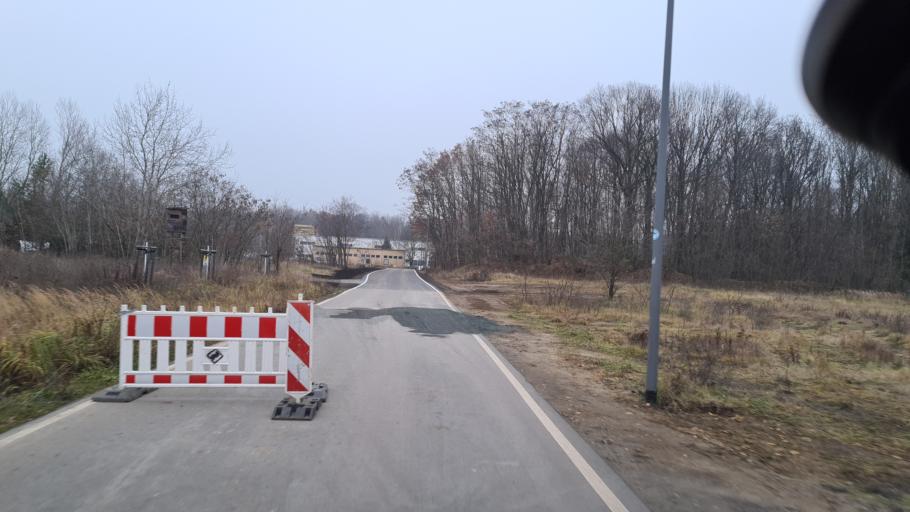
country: DE
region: Brandenburg
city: Sallgast
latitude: 51.5874
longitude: 13.7860
